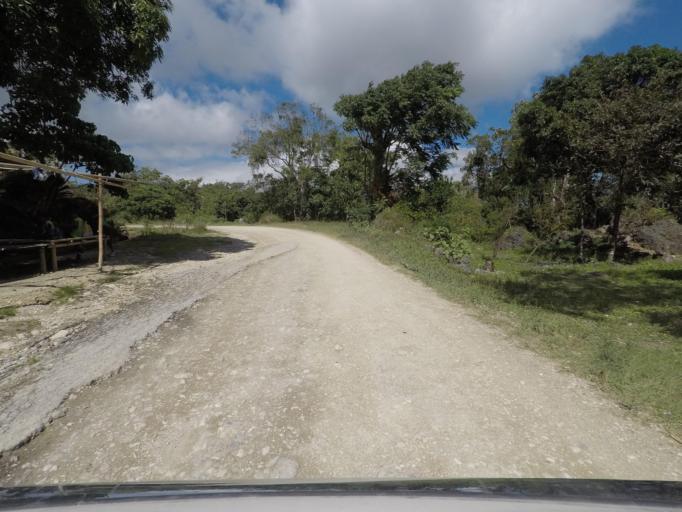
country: TL
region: Baucau
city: Venilale
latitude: -8.6810
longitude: 126.3724
